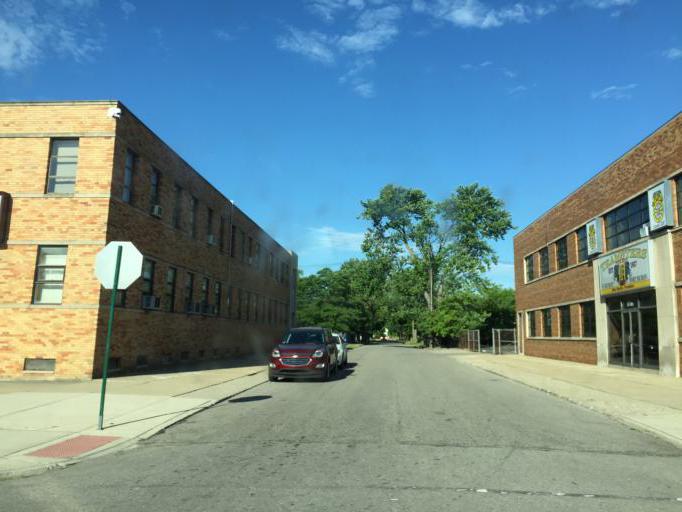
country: US
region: Michigan
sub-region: Wayne County
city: Detroit
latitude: 42.3372
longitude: -83.0702
